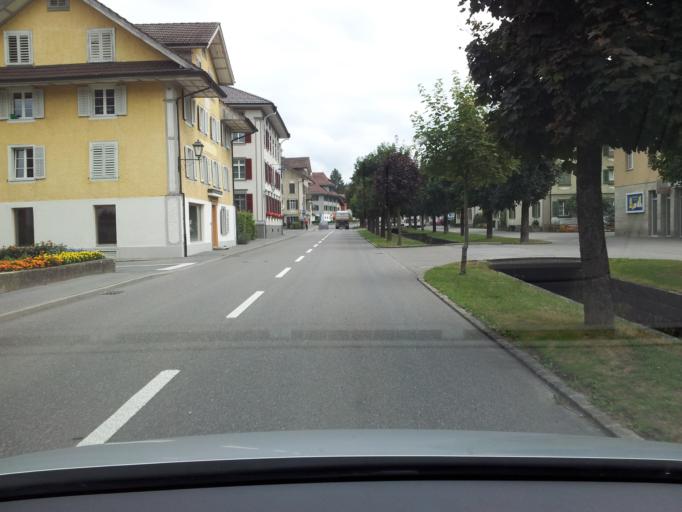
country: CH
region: Lucerne
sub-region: Sursee District
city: Buttisholz
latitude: 47.1142
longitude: 8.0922
